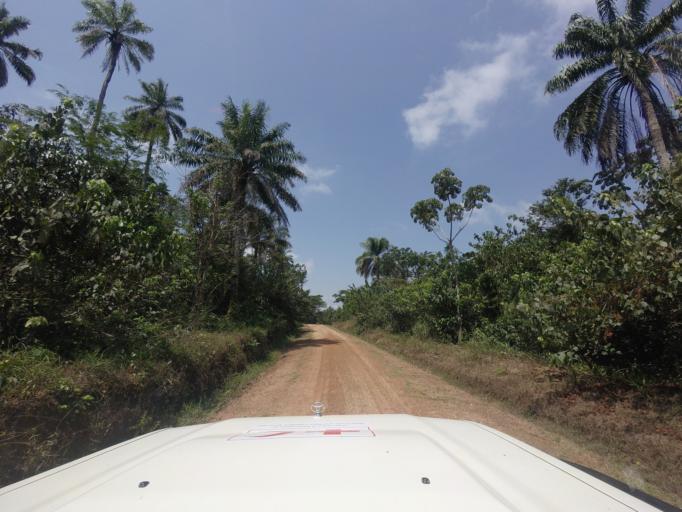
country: LR
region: Lofa
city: Voinjama
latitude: 8.4909
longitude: -9.6524
